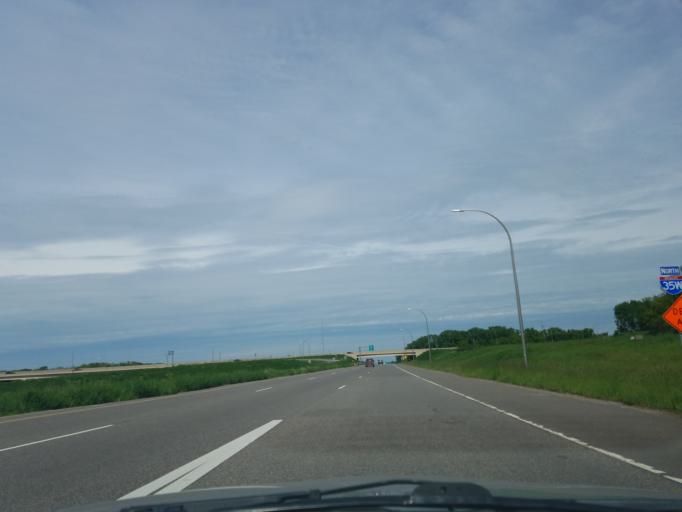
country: US
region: Minnesota
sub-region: Ramsey County
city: Arden Hills
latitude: 45.0617
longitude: -93.1541
